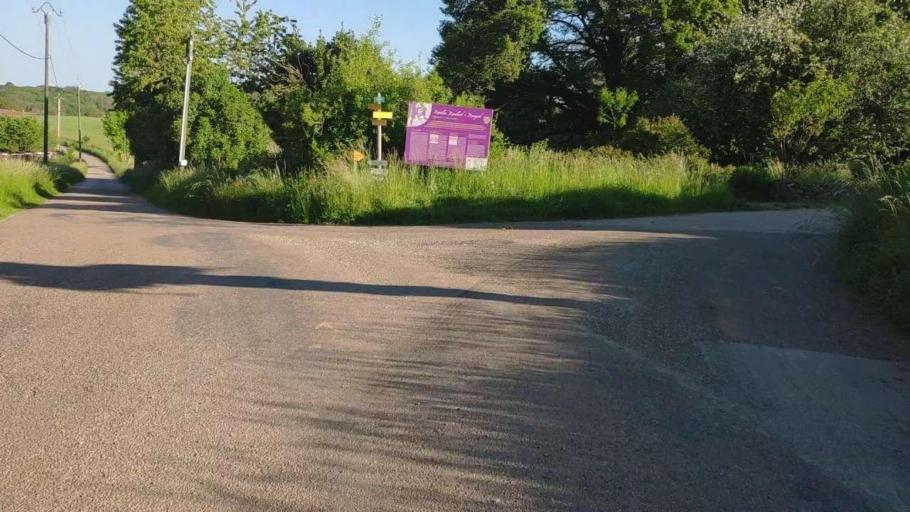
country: FR
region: Franche-Comte
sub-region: Departement du Jura
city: Perrigny
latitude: 46.7154
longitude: 5.6210
